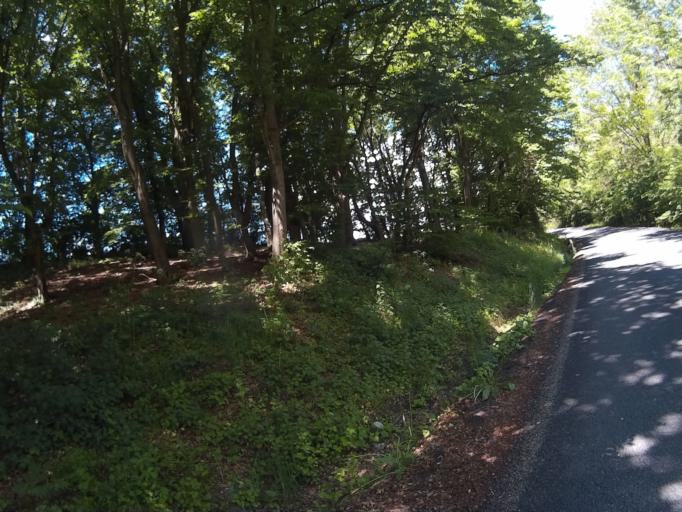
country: HU
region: Vas
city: Kormend
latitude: 46.9676
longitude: 16.5720
